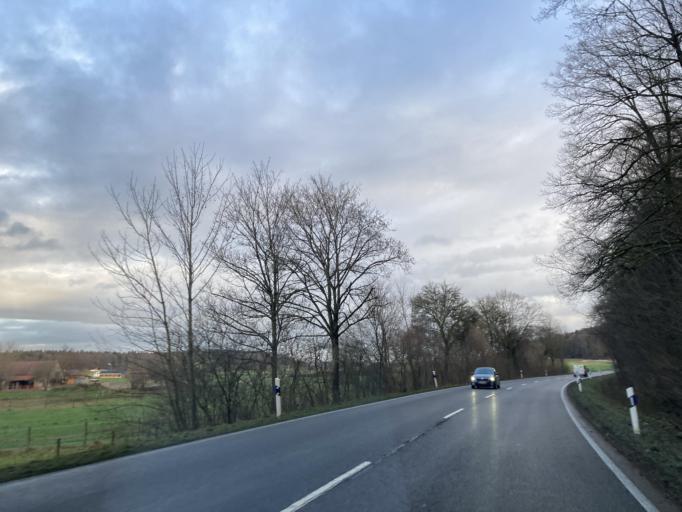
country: DE
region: Baden-Wuerttemberg
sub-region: Tuebingen Region
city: Bad Schussenried
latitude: 48.0247
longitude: 9.6625
